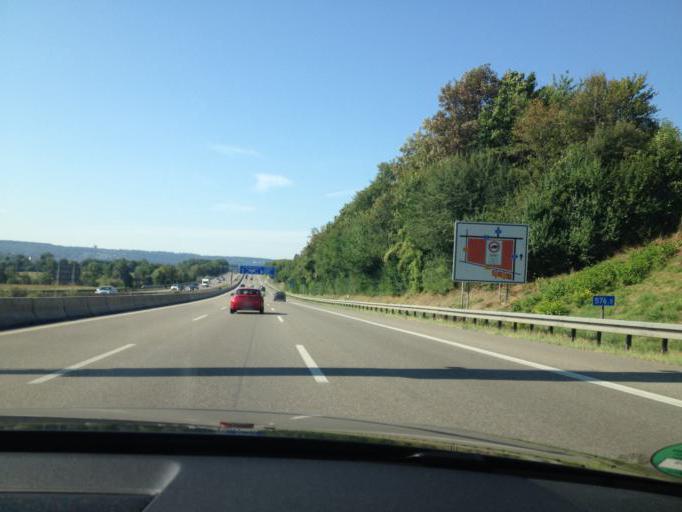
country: DE
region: Baden-Wuerttemberg
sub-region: Regierungsbezirk Stuttgart
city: Ditzingen
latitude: 48.8295
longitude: 9.0844
